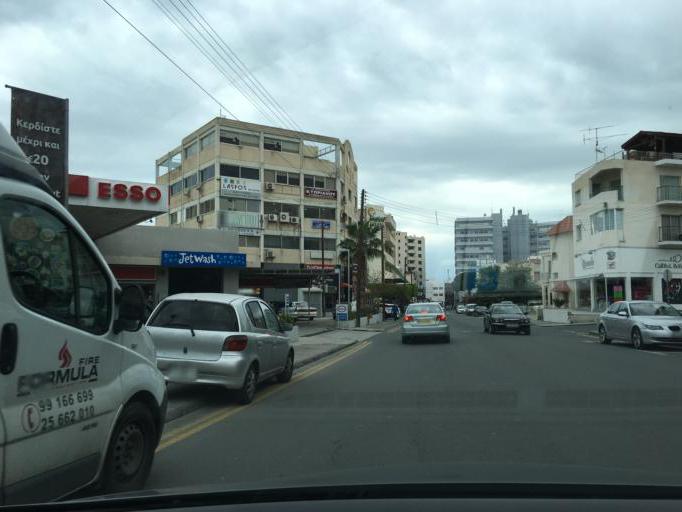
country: CY
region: Limassol
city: Limassol
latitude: 34.6832
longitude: 33.0441
